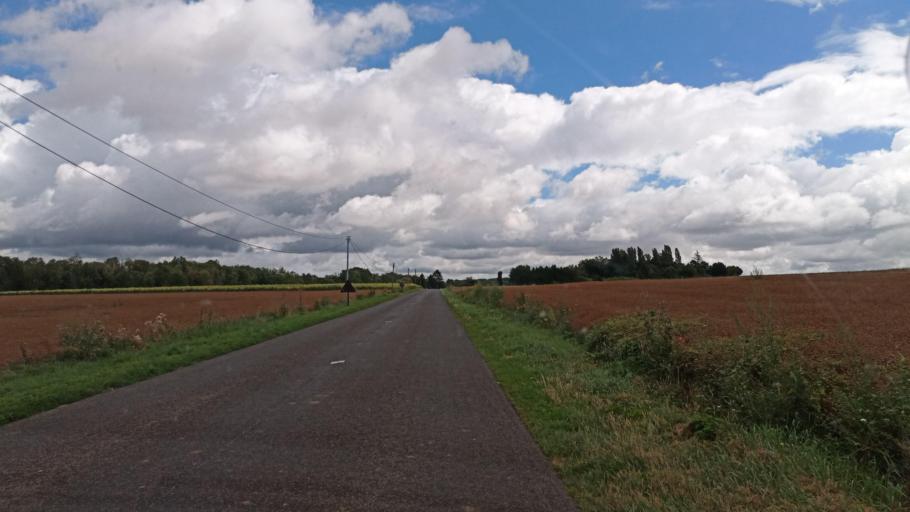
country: FR
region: Bourgogne
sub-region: Departement de l'Yonne
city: Cheroy
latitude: 48.2540
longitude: 3.0220
